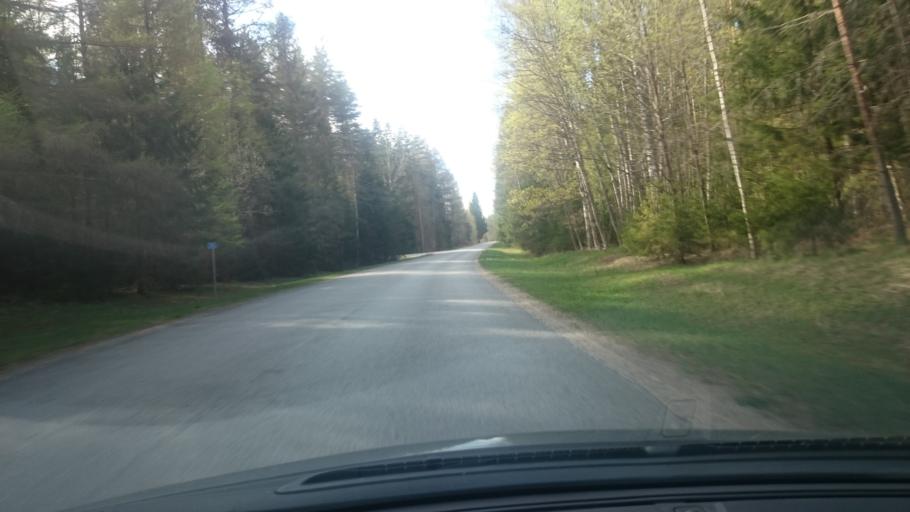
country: EE
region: Ida-Virumaa
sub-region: Toila vald
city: Voka
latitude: 59.1623
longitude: 27.5896
